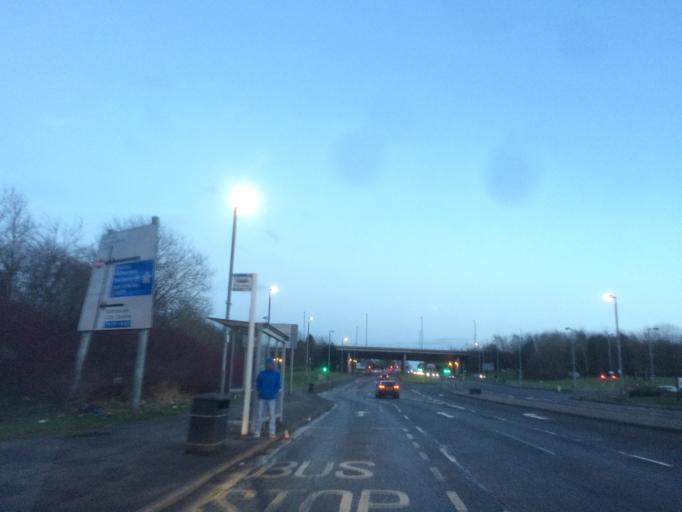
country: GB
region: Scotland
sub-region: East Renfrewshire
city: Newton Mearns
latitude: 55.8055
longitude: -4.3402
